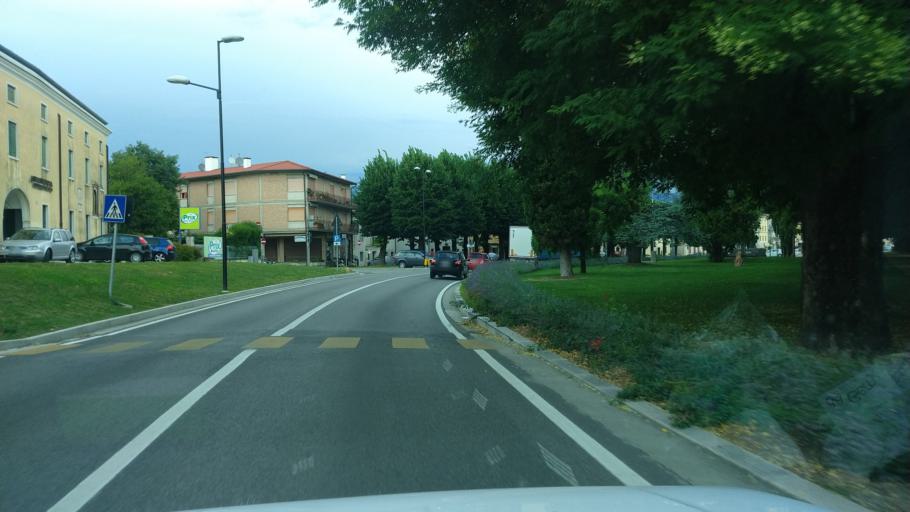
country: IT
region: Veneto
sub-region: Provincia di Vicenza
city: Nove
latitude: 45.7230
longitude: 11.6777
